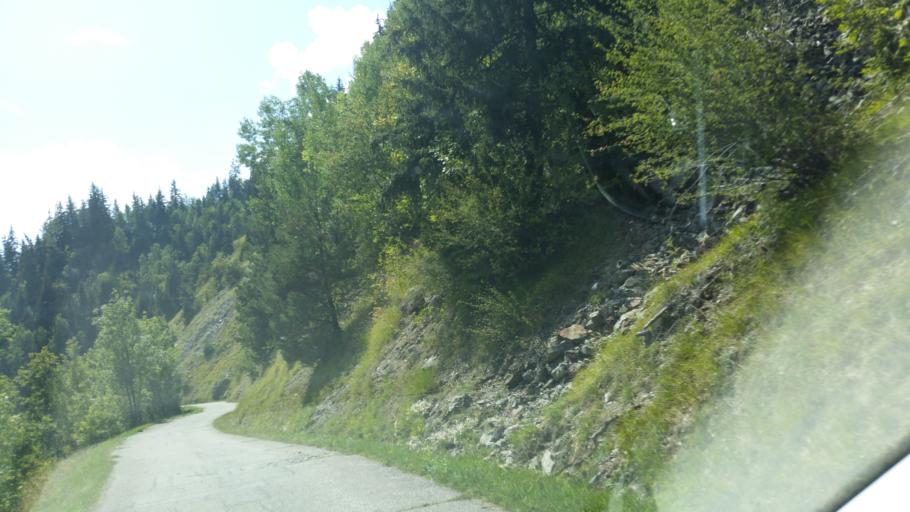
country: FR
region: Rhone-Alpes
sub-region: Departement de la Savoie
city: La Chambre
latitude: 45.4031
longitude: 6.3245
